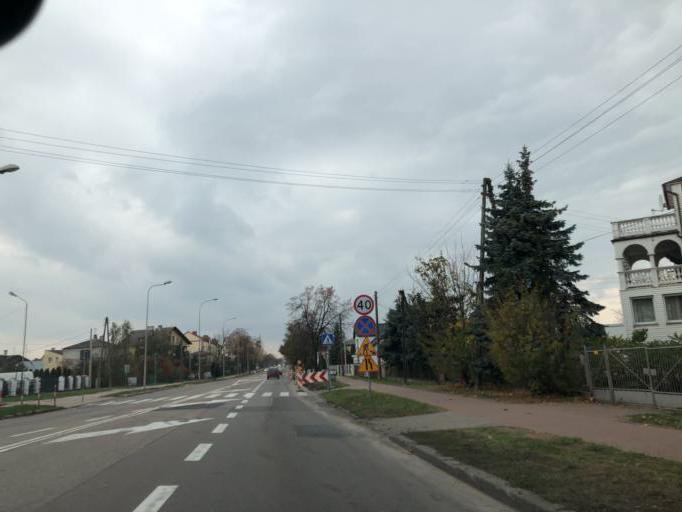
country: PL
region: Podlasie
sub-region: Lomza
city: Lomza
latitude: 53.1780
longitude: 22.0573
